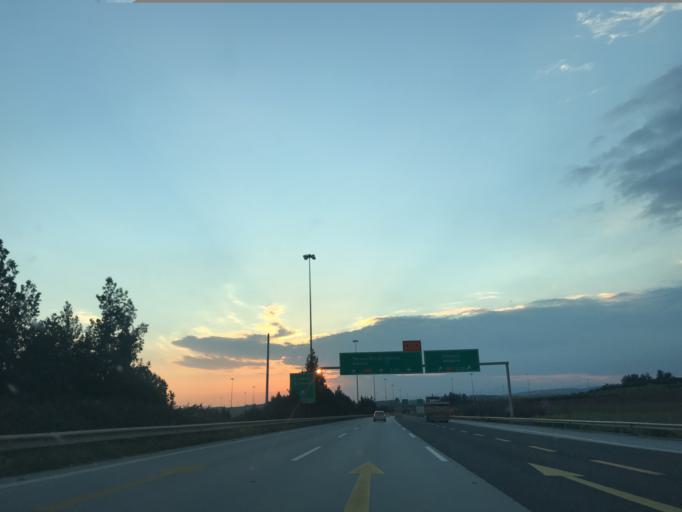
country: TR
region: Mersin
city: Yenice
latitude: 37.0089
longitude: 34.9757
